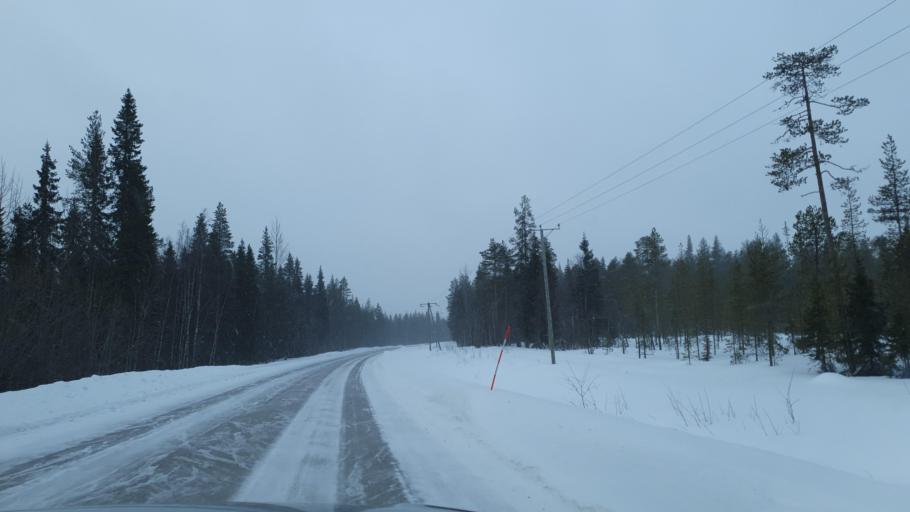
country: FI
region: Lapland
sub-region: Tunturi-Lappi
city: Kolari
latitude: 67.4461
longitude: 23.8430
